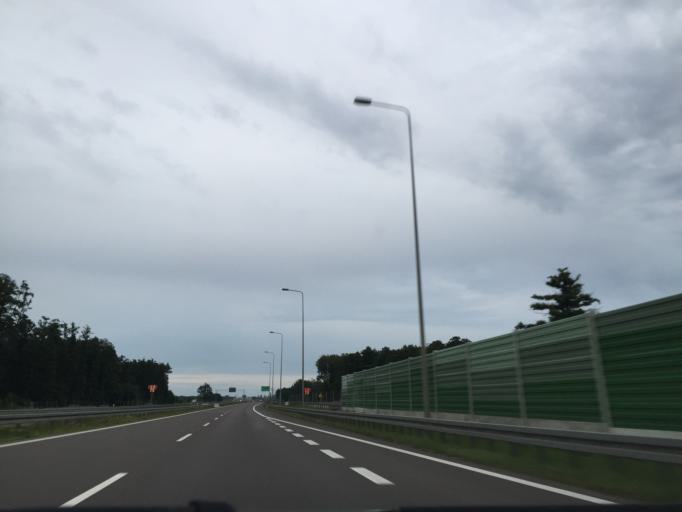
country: PL
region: Podlasie
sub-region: Powiat bialostocki
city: Tykocin
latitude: 53.1560
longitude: 22.8711
